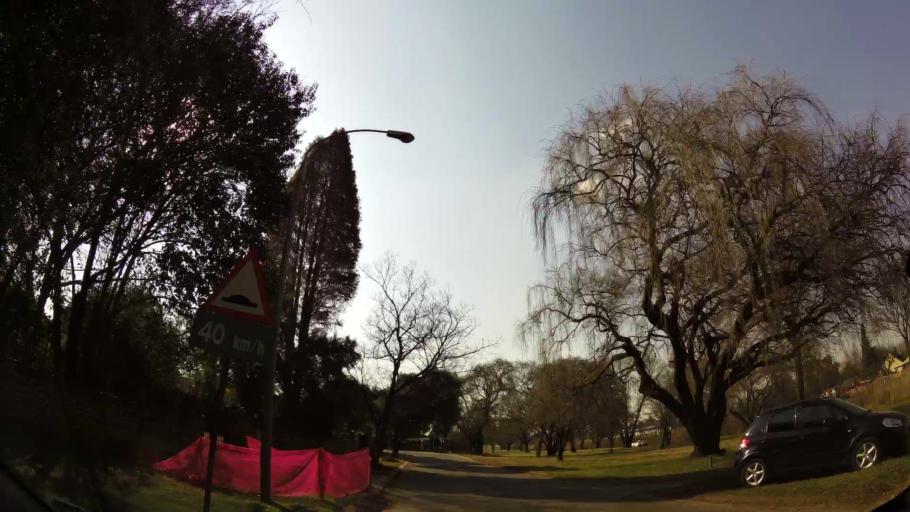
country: ZA
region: Gauteng
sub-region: Ekurhuleni Metropolitan Municipality
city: Benoni
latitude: -26.1564
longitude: 28.2872
